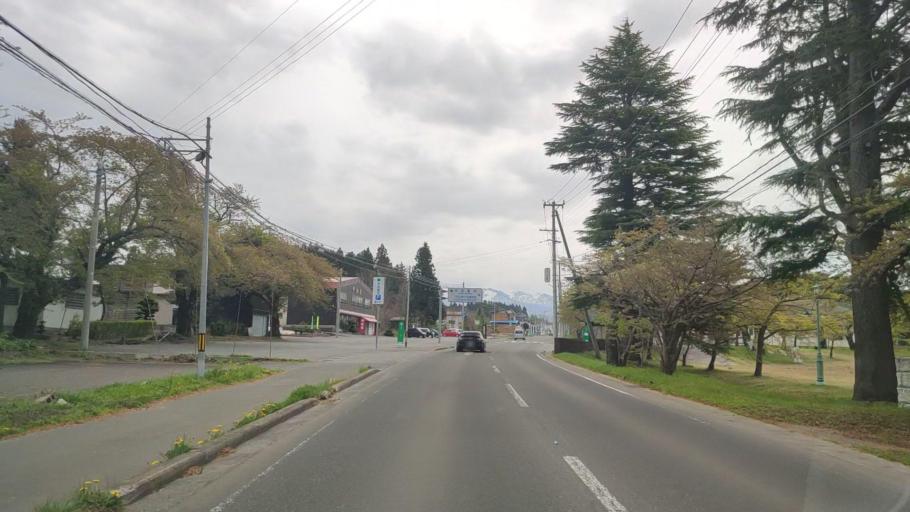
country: JP
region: Aomori
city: Aomori Shi
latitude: 40.7858
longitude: 140.7895
